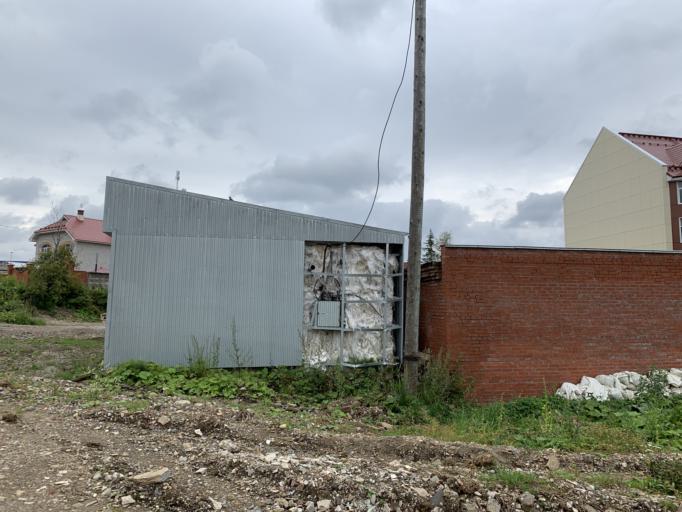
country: RU
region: Perm
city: Gubakha
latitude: 58.8307
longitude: 57.5607
